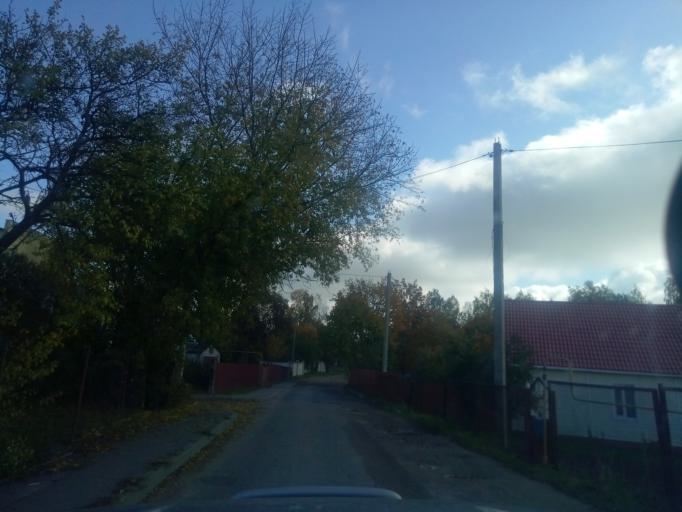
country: BY
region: Minsk
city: Zaslawye
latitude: 54.0087
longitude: 27.3058
